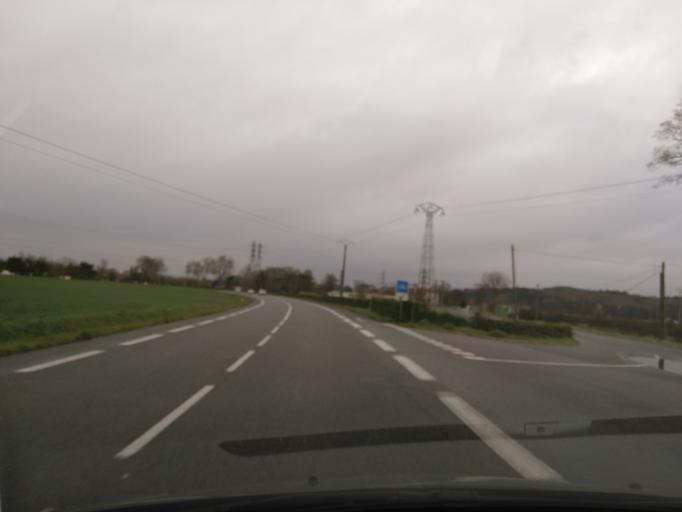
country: FR
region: Midi-Pyrenees
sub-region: Departement de la Haute-Garonne
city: Carbonne
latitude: 43.2828
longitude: 1.2155
